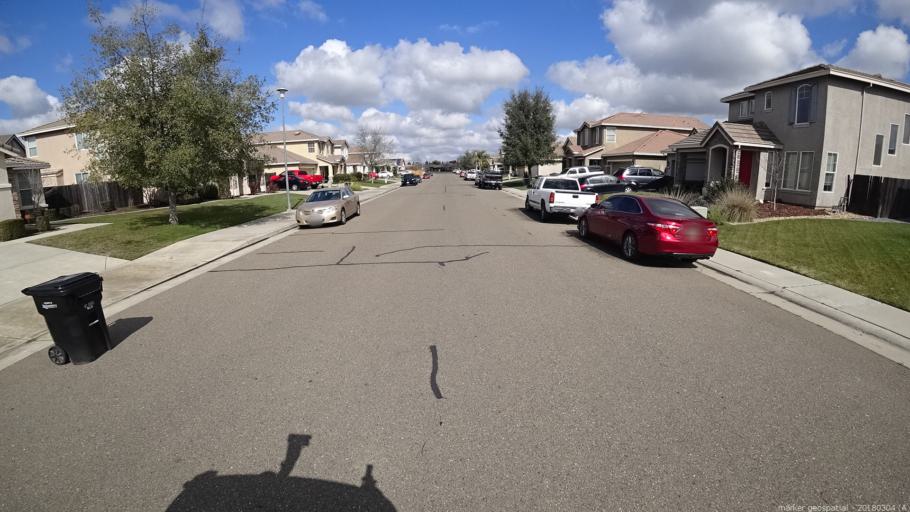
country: US
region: California
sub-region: Sacramento County
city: Vineyard
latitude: 38.4543
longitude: -121.3240
